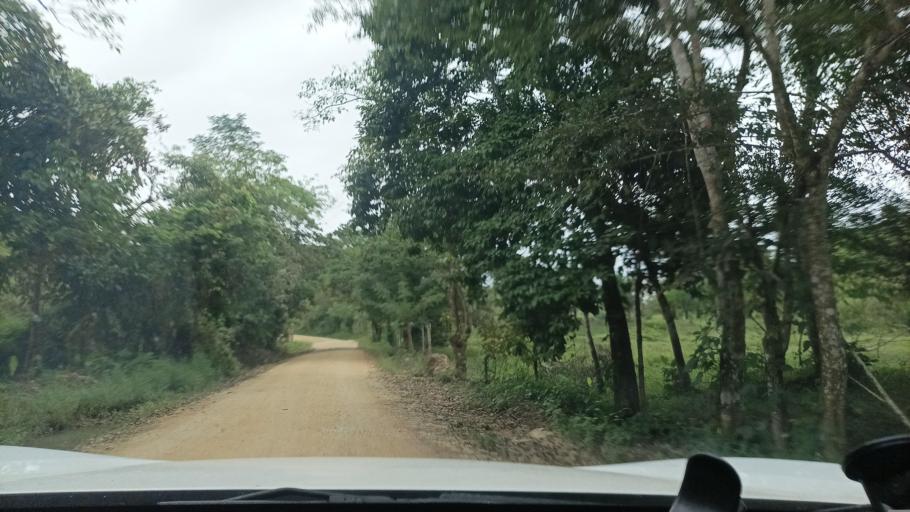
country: MX
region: Veracruz
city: Hidalgotitlan
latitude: 17.6063
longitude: -94.5258
